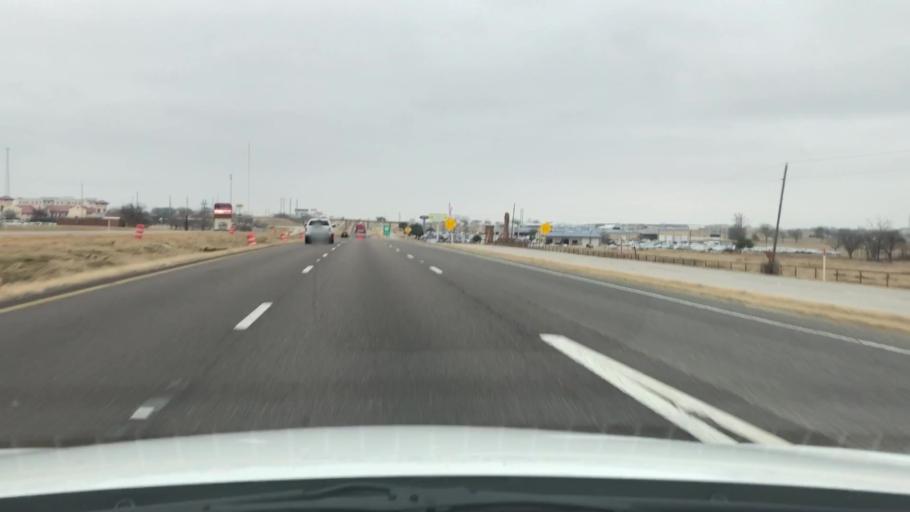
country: US
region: Texas
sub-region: Cooke County
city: Gainesville
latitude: 33.6758
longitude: -97.1528
